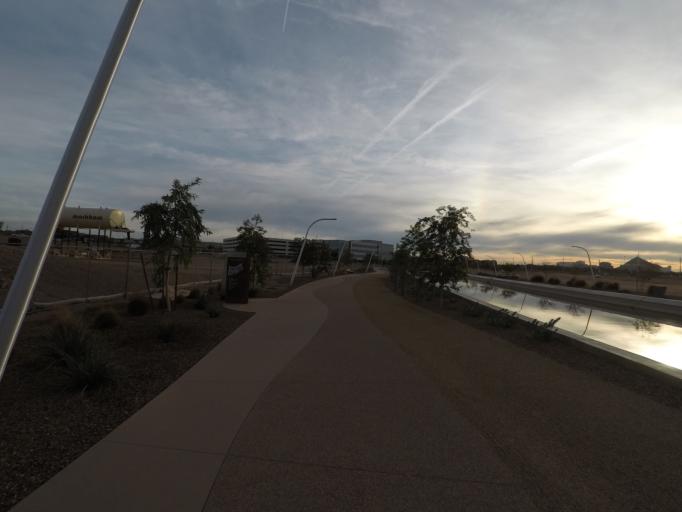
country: US
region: Arizona
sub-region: Maricopa County
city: Tempe Junction
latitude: 33.4396
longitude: -111.9592
